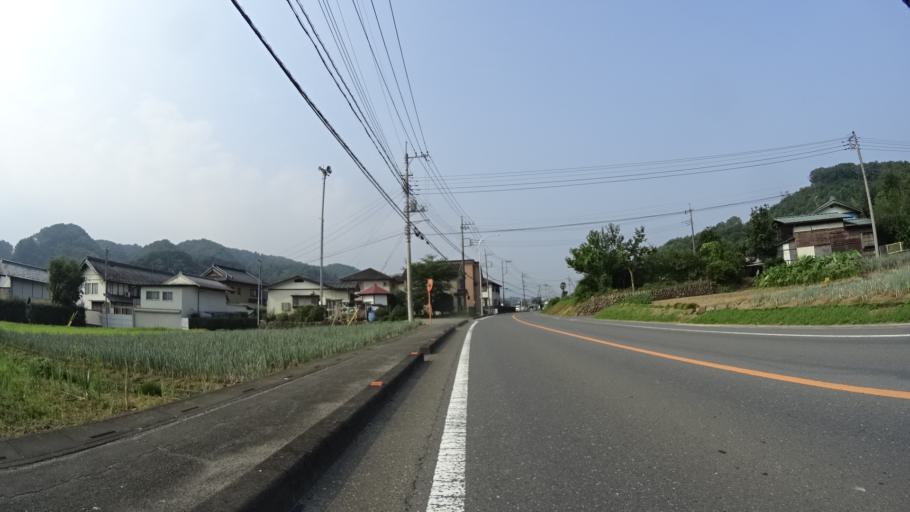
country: JP
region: Saitama
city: Chichibu
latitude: 36.0213
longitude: 139.0664
